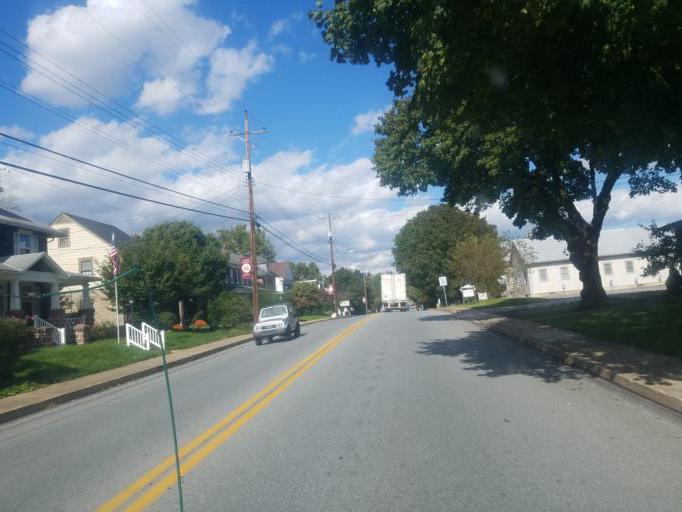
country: US
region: Pennsylvania
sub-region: York County
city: Emigsville
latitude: 40.0151
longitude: -76.7299
